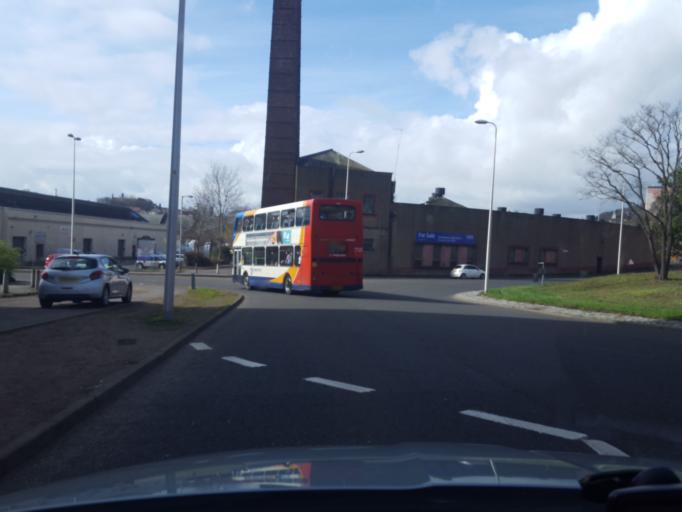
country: GB
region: Scotland
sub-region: Dundee City
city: Dundee
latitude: 56.4636
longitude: -2.9788
